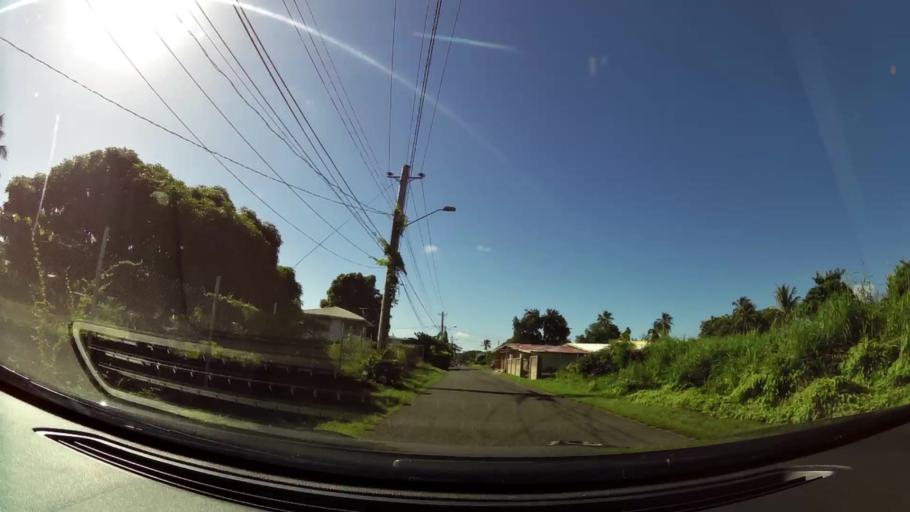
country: TT
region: Tobago
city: Scarborough
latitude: 11.1614
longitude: -60.8066
